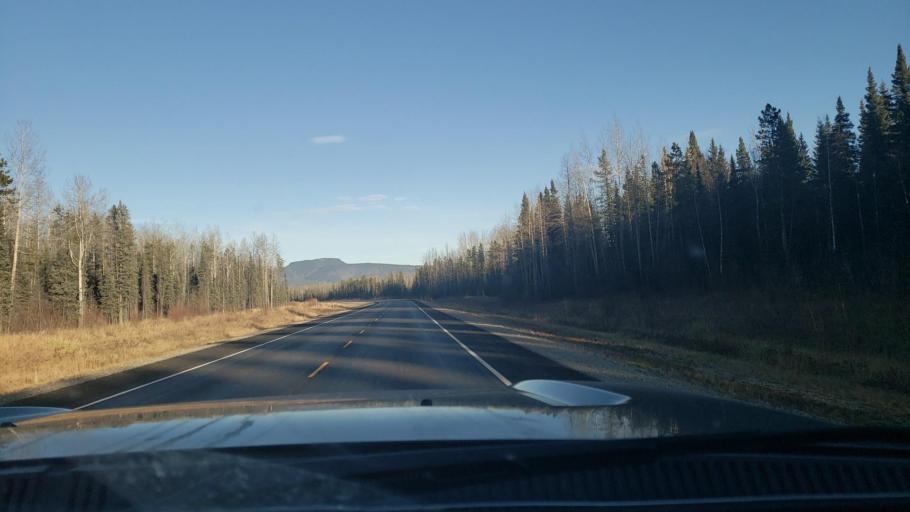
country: CA
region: British Columbia
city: Fort Nelson
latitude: 58.6600
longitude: -124.1170
